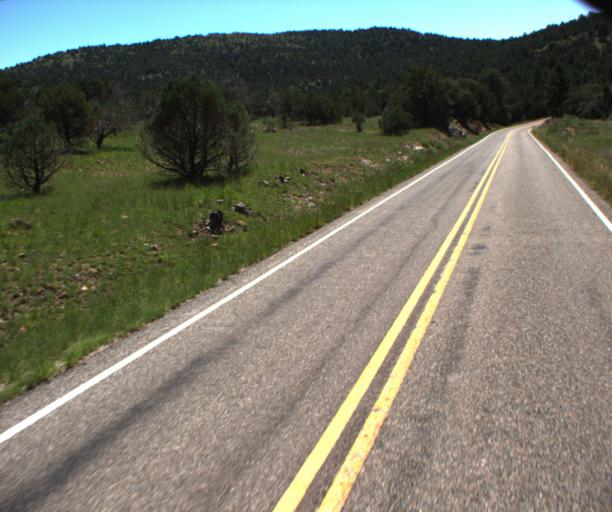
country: US
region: Arizona
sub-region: Greenlee County
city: Morenci
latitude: 33.2850
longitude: -109.3552
